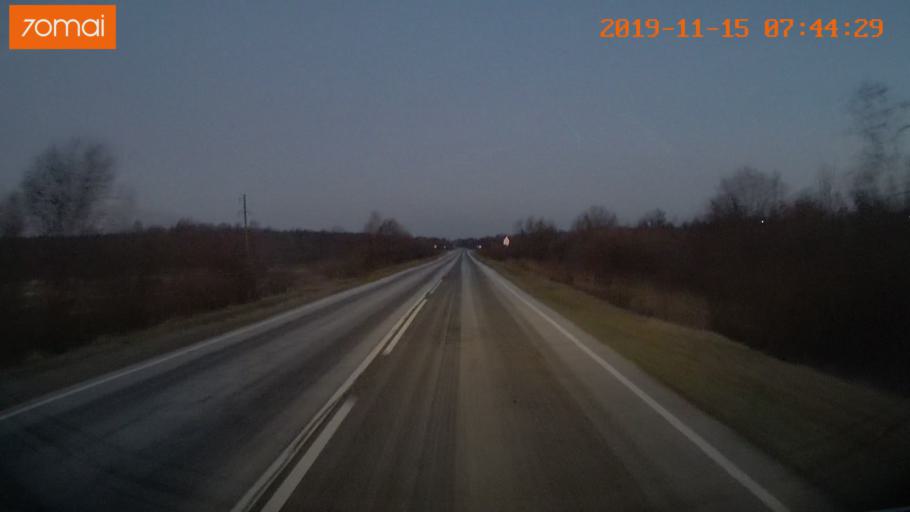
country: RU
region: Vologda
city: Sheksna
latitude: 58.8137
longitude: 38.3126
